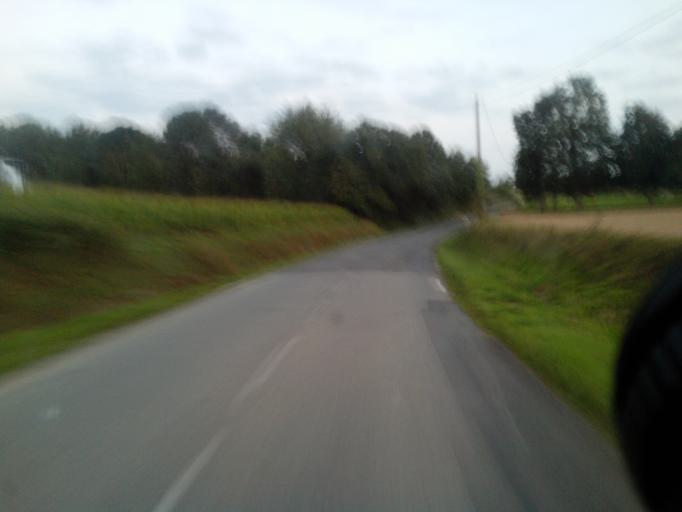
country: FR
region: Brittany
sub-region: Departement d'Ille-et-Vilaine
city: Iffendic
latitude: 48.1192
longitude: -2.0355
